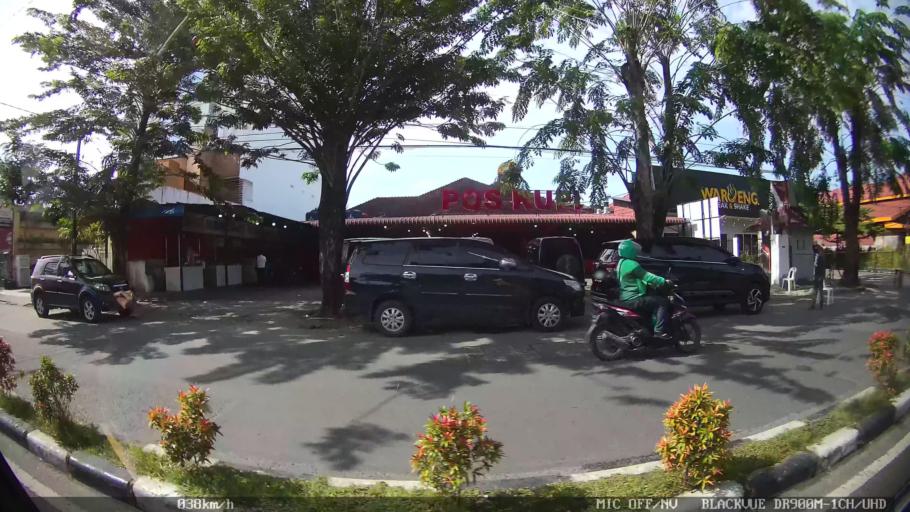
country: ID
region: North Sumatra
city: Medan
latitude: 3.5676
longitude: 98.6460
